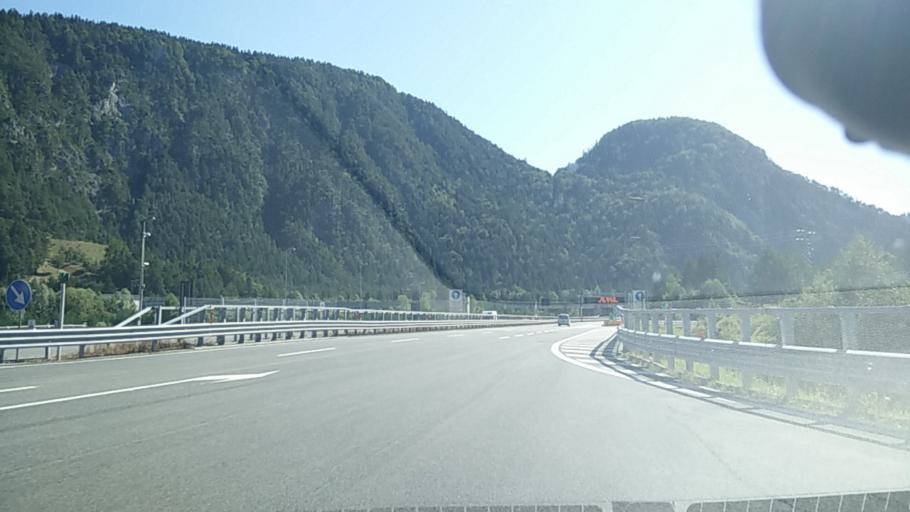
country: IT
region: Friuli Venezia Giulia
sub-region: Provincia di Udine
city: Malborghetto
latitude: 46.5067
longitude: 13.4818
